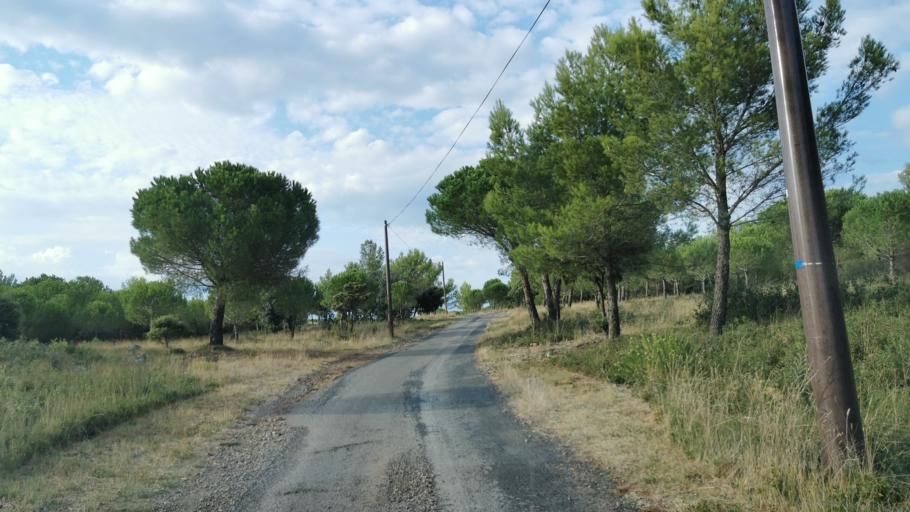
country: FR
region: Languedoc-Roussillon
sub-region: Departement de l'Aude
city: Bizanet
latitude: 43.1761
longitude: 2.8914
